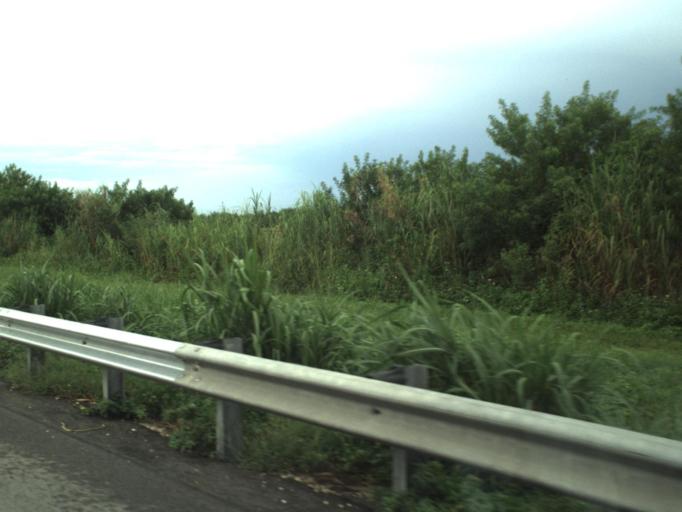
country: US
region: Florida
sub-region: Miami-Dade County
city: The Hammocks
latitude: 25.6663
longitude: -80.4810
